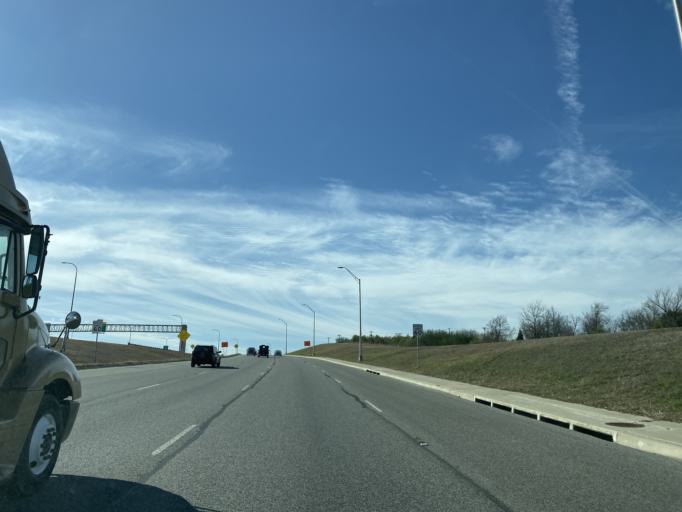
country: US
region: Texas
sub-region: Travis County
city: Manor
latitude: 30.3445
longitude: -97.5823
